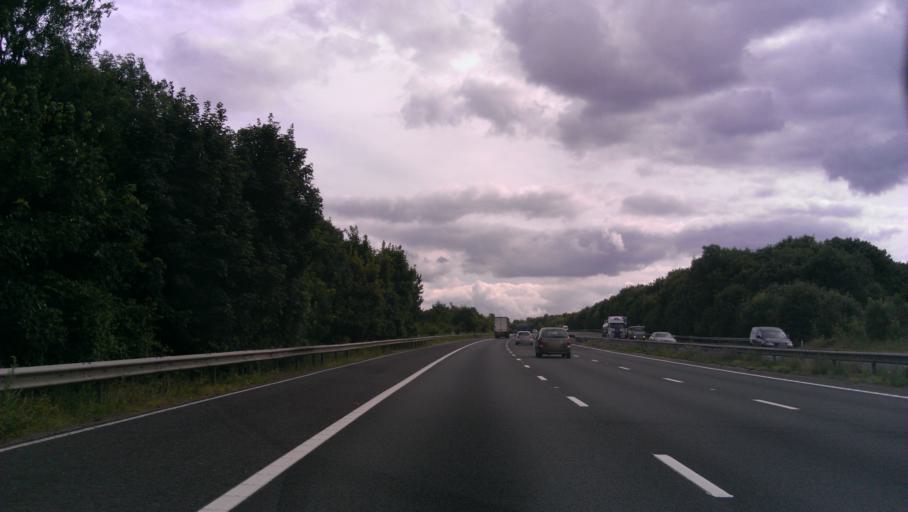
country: GB
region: England
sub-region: Kent
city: Borough Green
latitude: 51.3411
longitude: 0.2758
